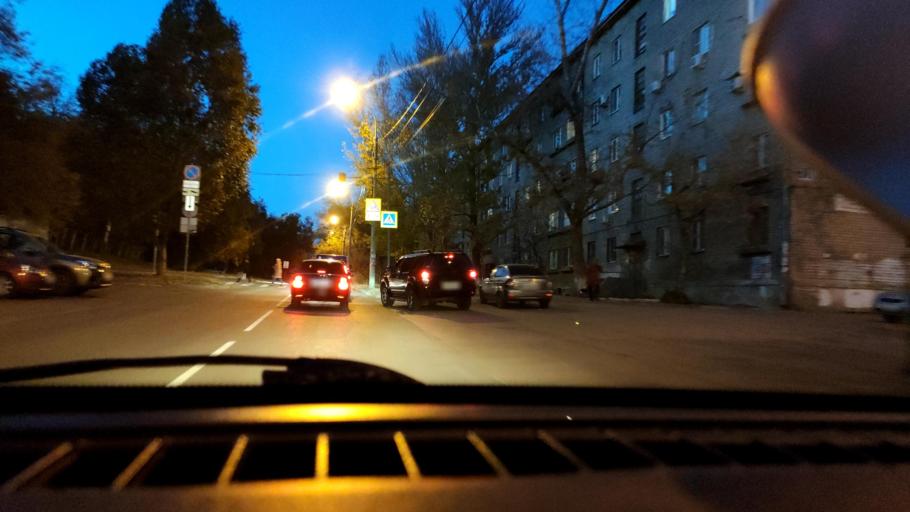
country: RU
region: Samara
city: Samara
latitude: 53.2097
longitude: 50.2207
